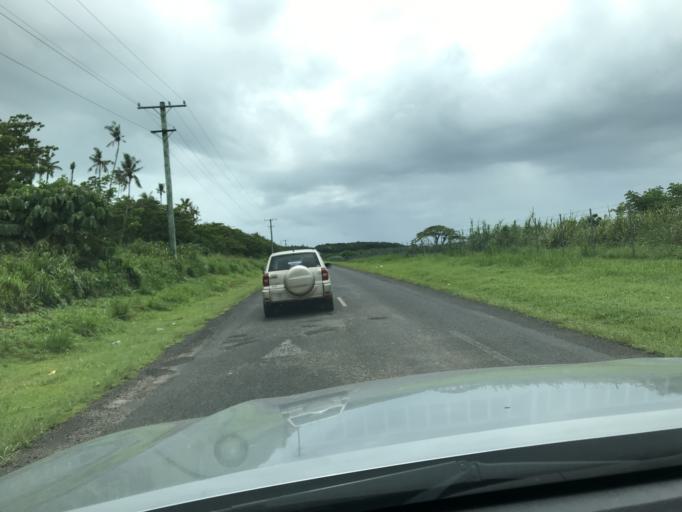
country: WS
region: A'ana
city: Satapuala
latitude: -13.8338
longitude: -172.0029
